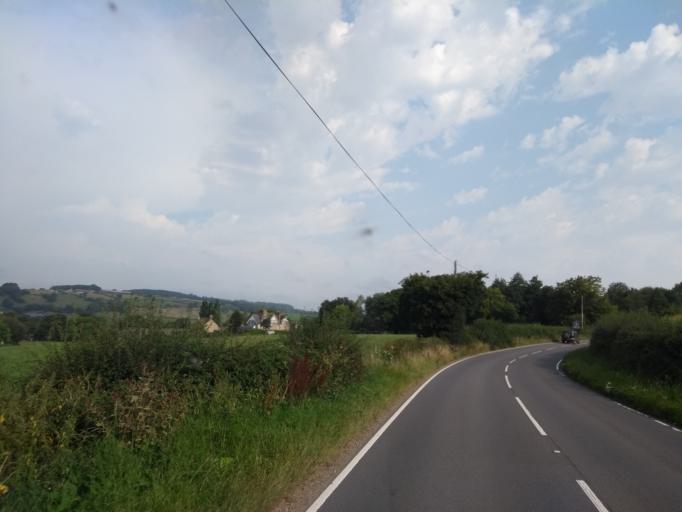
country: GB
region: England
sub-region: Devon
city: Axminster
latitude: 50.7565
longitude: -3.0243
